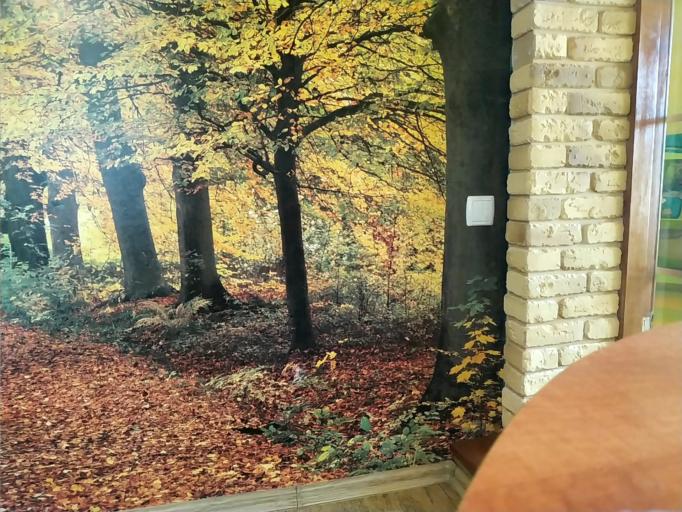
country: RU
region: Arkhangelskaya
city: Onega
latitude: 63.7378
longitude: 38.0805
